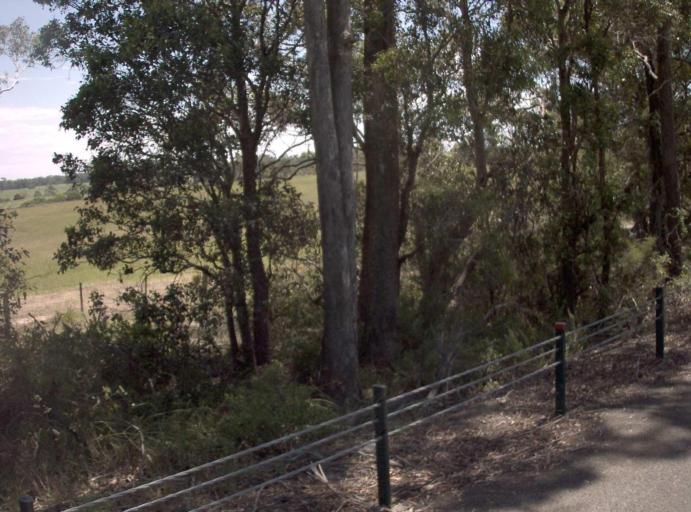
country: AU
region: Victoria
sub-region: East Gippsland
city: Lakes Entrance
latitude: -37.8366
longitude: 148.0321
